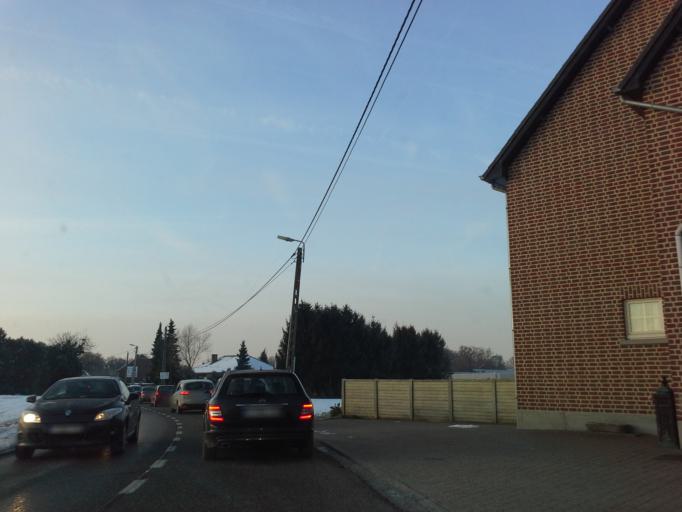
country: BE
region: Flanders
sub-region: Provincie Vlaams-Brabant
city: Bierbeek
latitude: 50.8603
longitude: 4.7826
